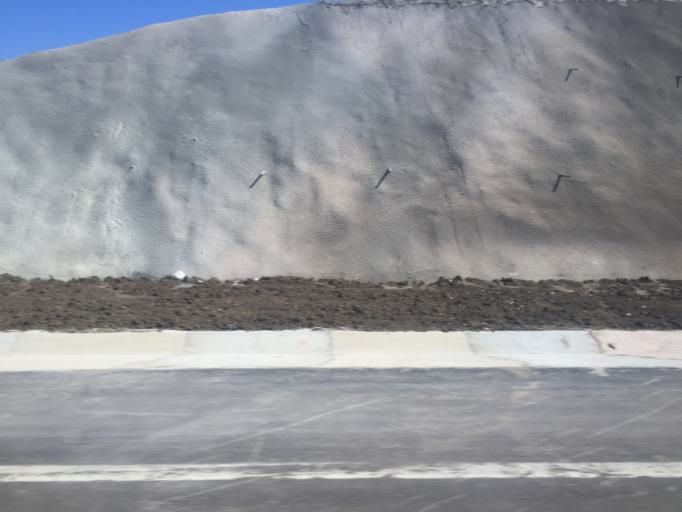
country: TR
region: Bursa
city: Mahmudiye
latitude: 40.2667
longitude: 28.6416
